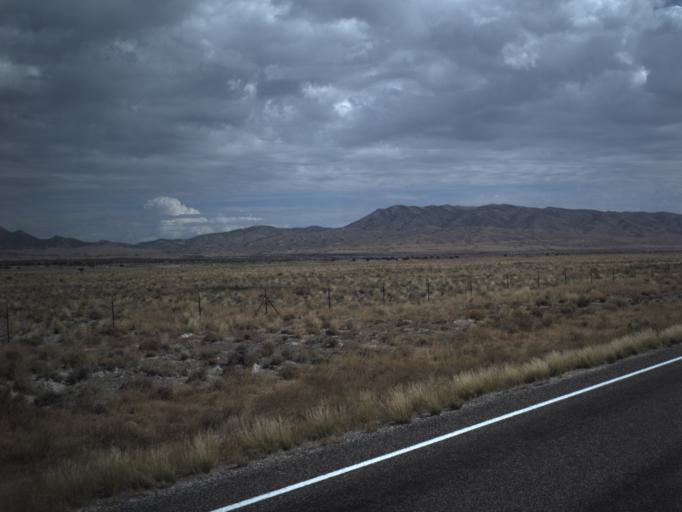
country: US
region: Utah
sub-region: Tooele County
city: Wendover
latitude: 41.4301
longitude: -113.8072
